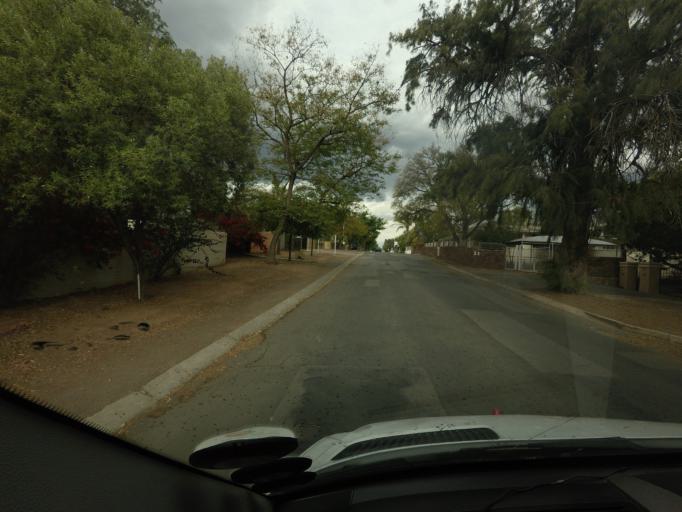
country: ZA
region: Western Cape
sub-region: Eden District Municipality
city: Oudtshoorn
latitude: -33.5839
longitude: 22.2024
